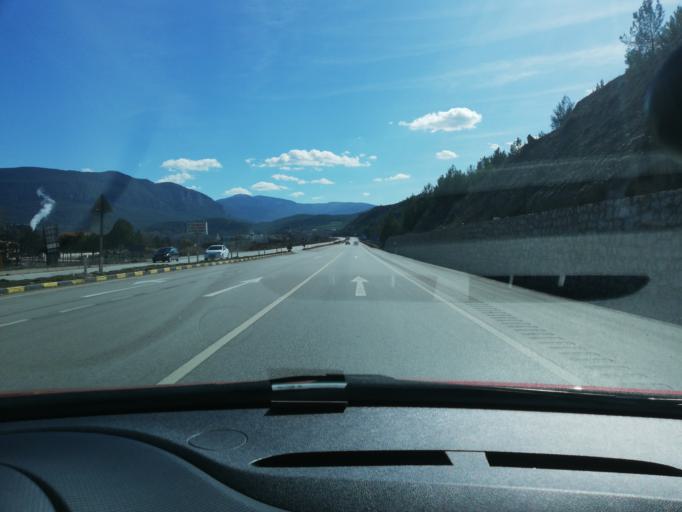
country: TR
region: Karabuk
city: Karabuk
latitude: 41.1452
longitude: 32.6667
